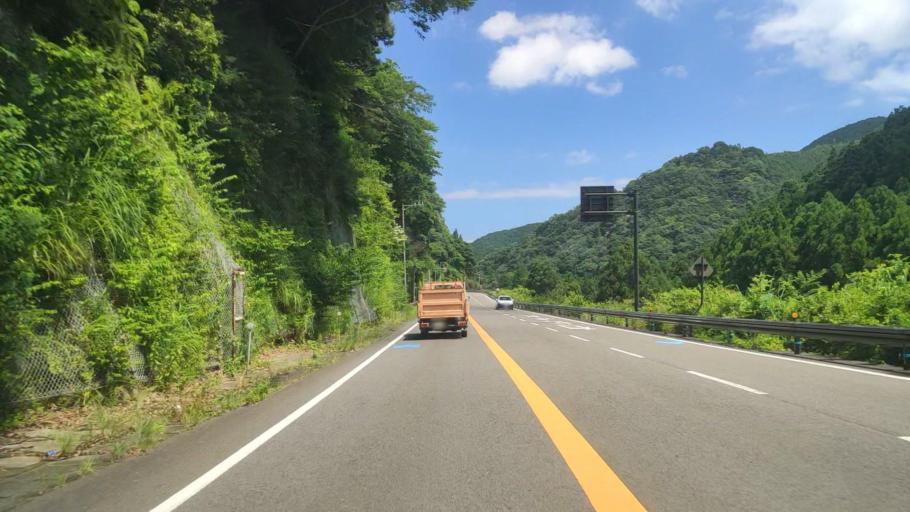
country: JP
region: Mie
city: Owase
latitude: 33.9239
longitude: 136.0940
